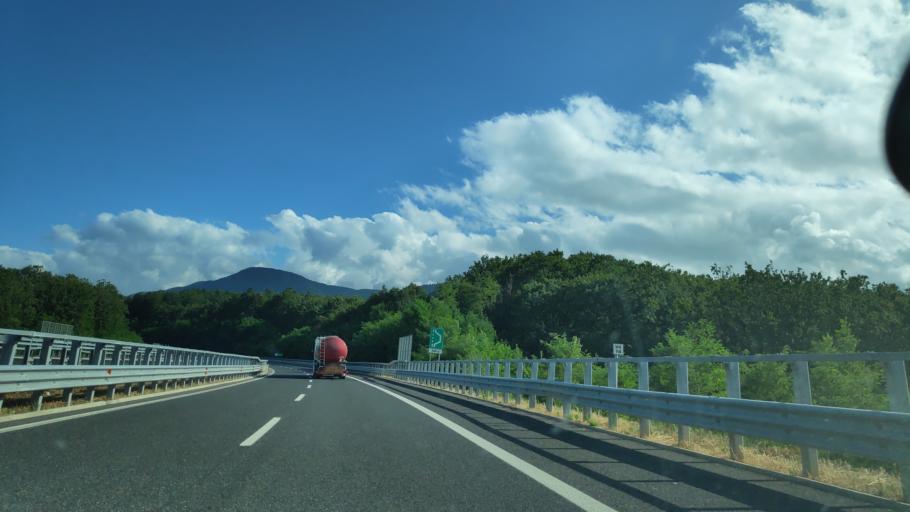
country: IT
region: Campania
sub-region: Provincia di Salerno
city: Casalbuono
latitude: 40.2406
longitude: 15.6596
